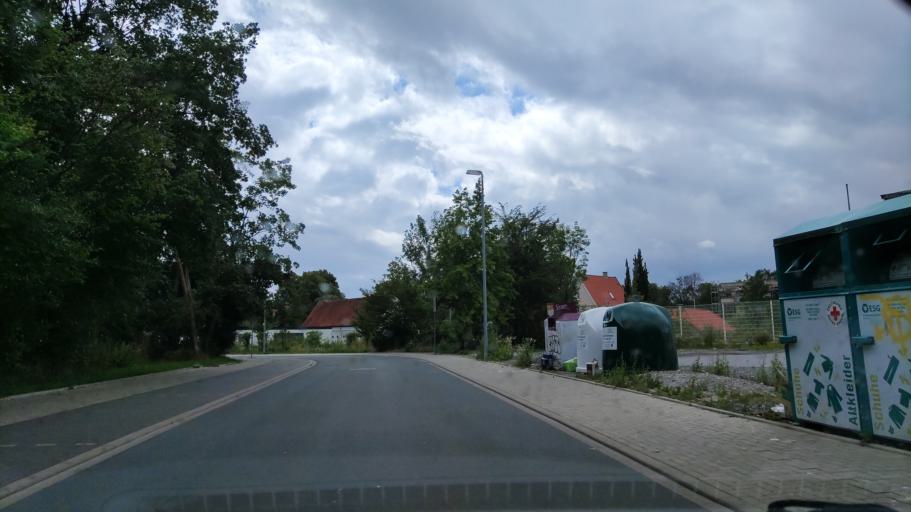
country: DE
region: North Rhine-Westphalia
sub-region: Regierungsbezirk Arnsberg
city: Soest
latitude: 51.5792
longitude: 8.0973
